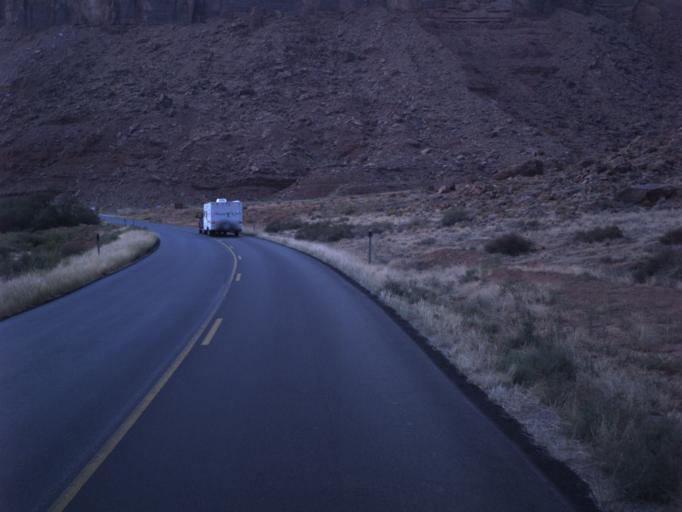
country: US
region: Utah
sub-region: Grand County
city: Moab
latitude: 38.6469
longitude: -109.4768
